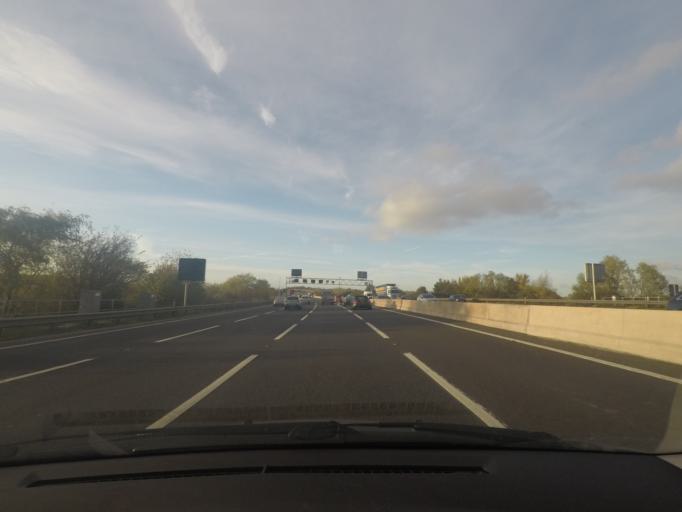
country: GB
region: England
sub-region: City and Borough of Wakefield
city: Crigglestone
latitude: 53.6569
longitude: -1.5293
